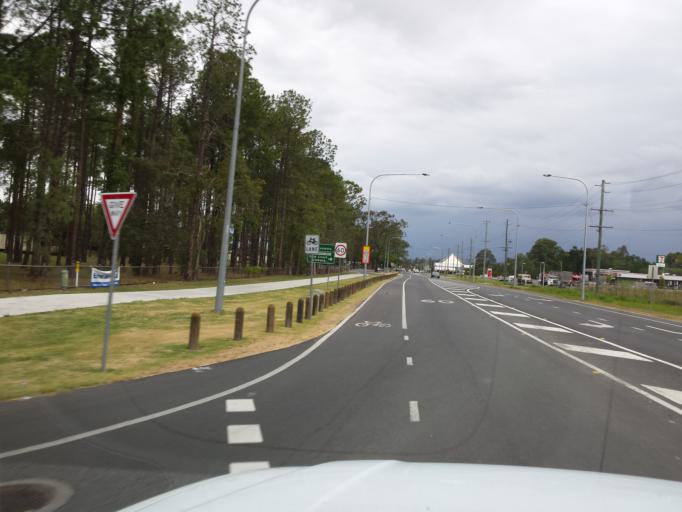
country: AU
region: Queensland
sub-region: Gold Coast
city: Oxenford
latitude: -27.8667
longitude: 153.3154
